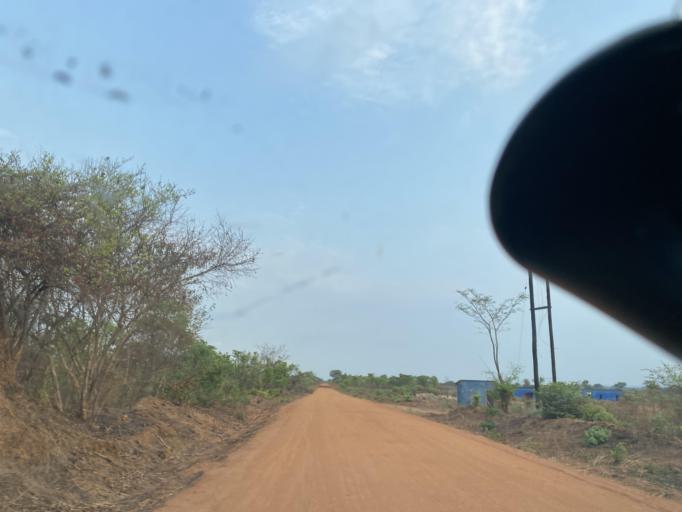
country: ZM
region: Lusaka
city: Chongwe
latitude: -15.2328
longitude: 28.5890
